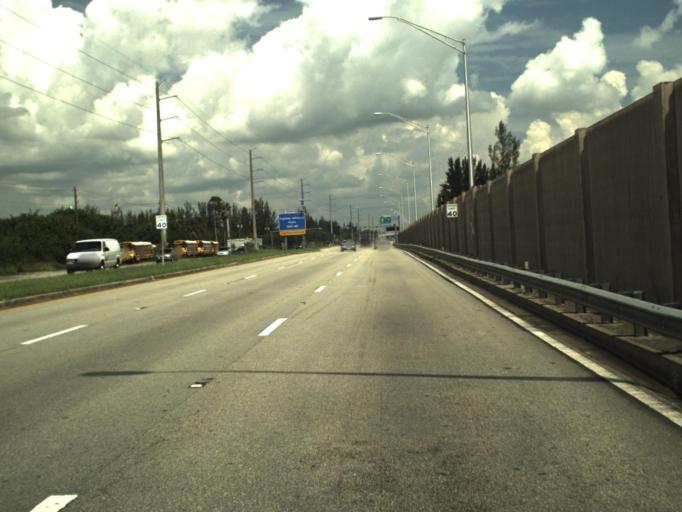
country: US
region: Florida
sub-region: Miami-Dade County
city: Tamiami
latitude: 25.7699
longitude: -80.4171
